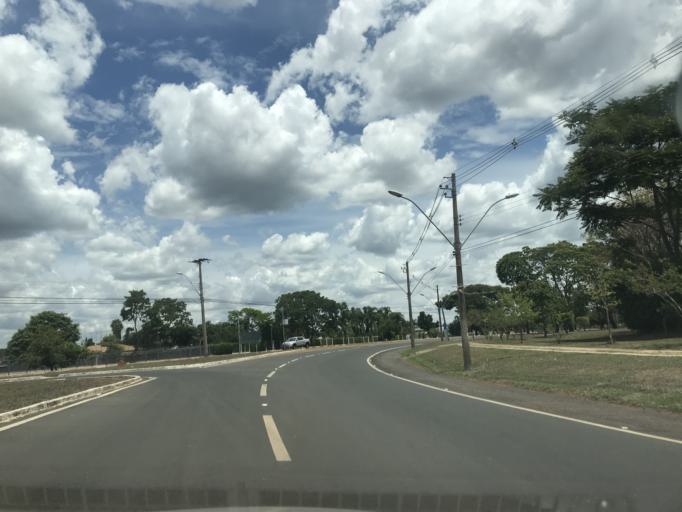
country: BR
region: Federal District
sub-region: Brasilia
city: Brasilia
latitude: -15.9092
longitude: -47.9468
